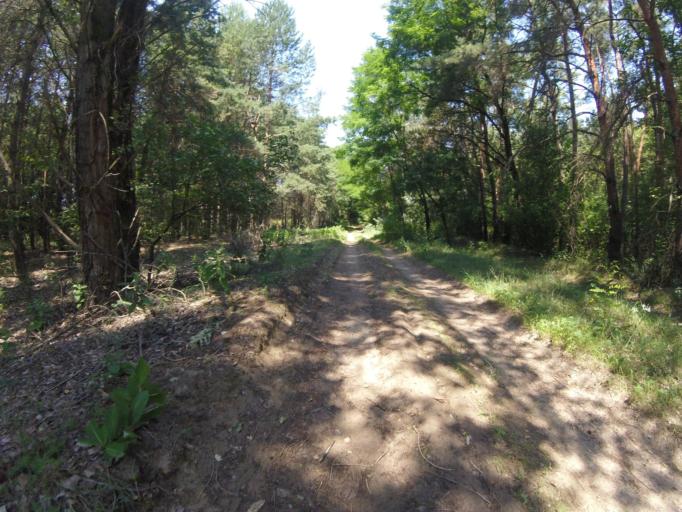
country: HU
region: Bacs-Kiskun
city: Jaszszentlaszlo
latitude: 46.6213
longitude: 19.7174
